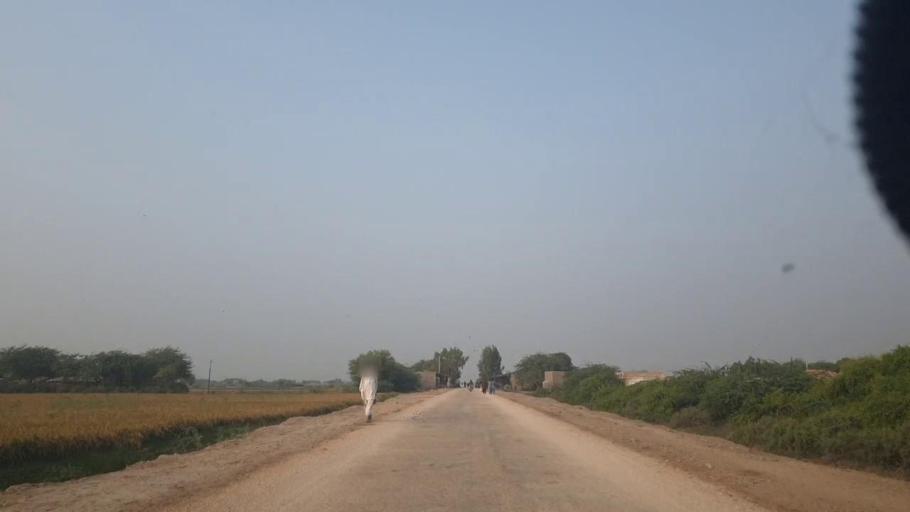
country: PK
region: Sindh
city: Bulri
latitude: 24.8367
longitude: 68.4033
